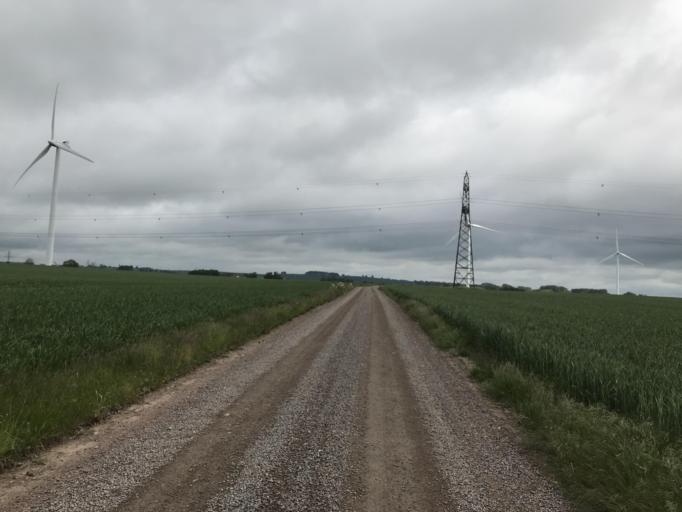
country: SE
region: Skane
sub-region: Landskrona
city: Asmundtorp
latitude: 55.8721
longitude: 12.8972
